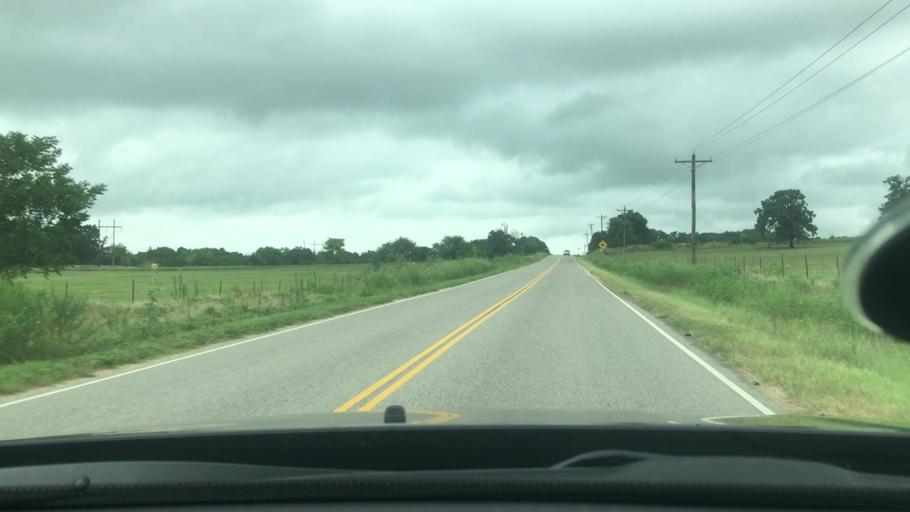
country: US
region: Oklahoma
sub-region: Bryan County
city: Calera
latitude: 33.9669
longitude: -96.5005
